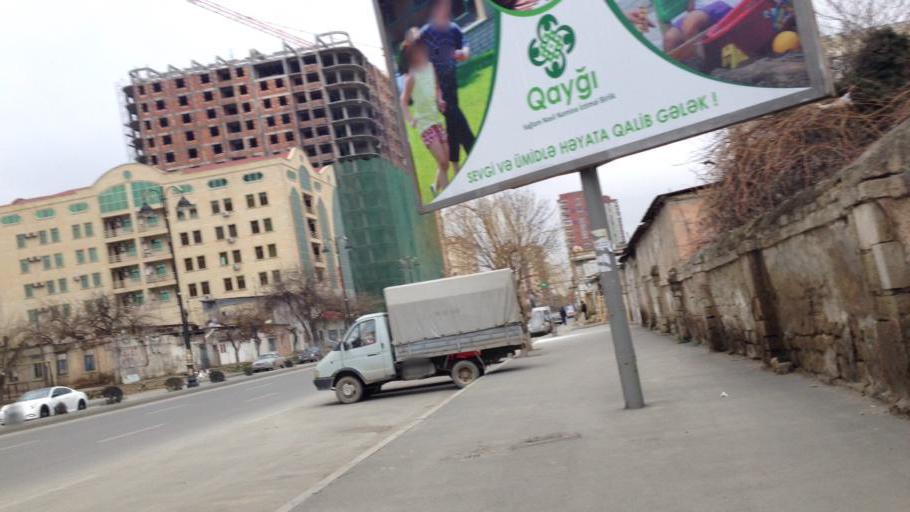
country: AZ
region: Baki
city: Baku
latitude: 40.3976
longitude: 49.8434
